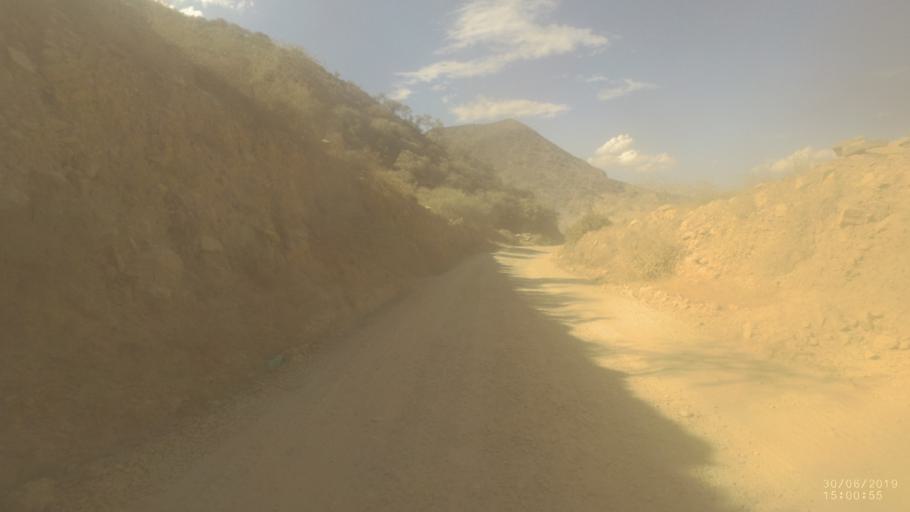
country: BO
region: Cochabamba
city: Irpa Irpa
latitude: -17.7346
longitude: -66.3388
